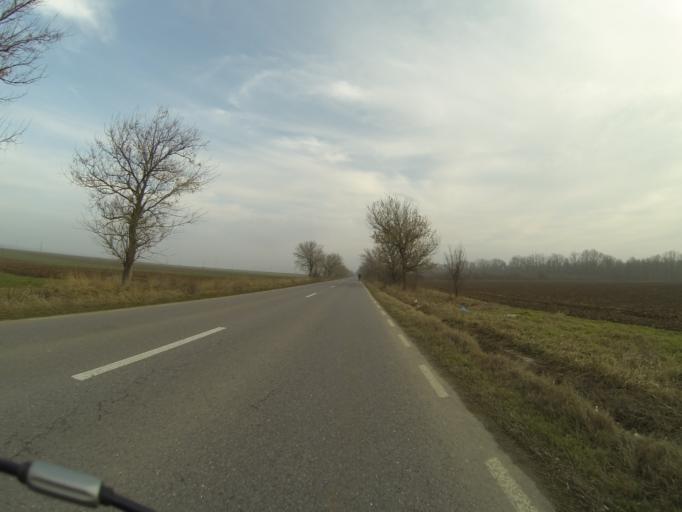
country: RO
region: Mehedinti
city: Vanju-Mare
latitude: 44.4049
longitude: 22.8976
